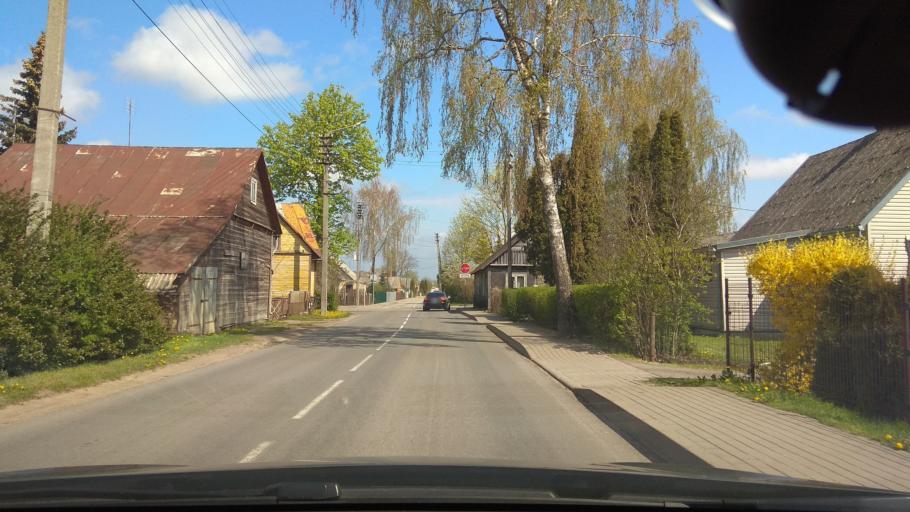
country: LT
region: Siauliu apskritis
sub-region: Joniskis
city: Joniskis
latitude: 56.2383
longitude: 23.6231
